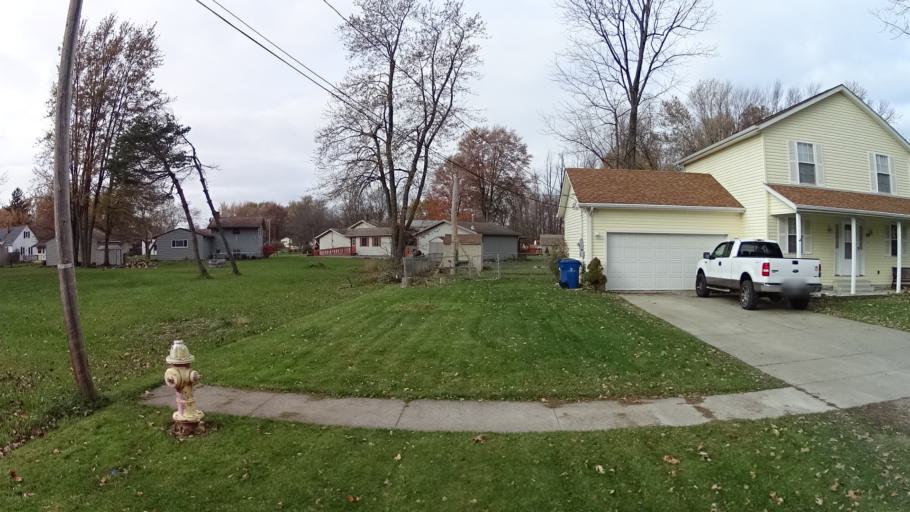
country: US
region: Ohio
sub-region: Lorain County
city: Sheffield Lake
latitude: 41.4867
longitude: -82.1174
